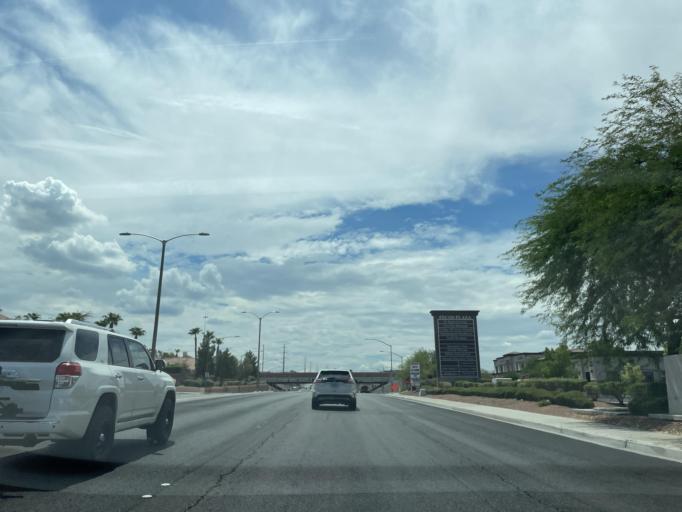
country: US
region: Nevada
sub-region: Clark County
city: Whitney
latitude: 36.0266
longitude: -115.1006
